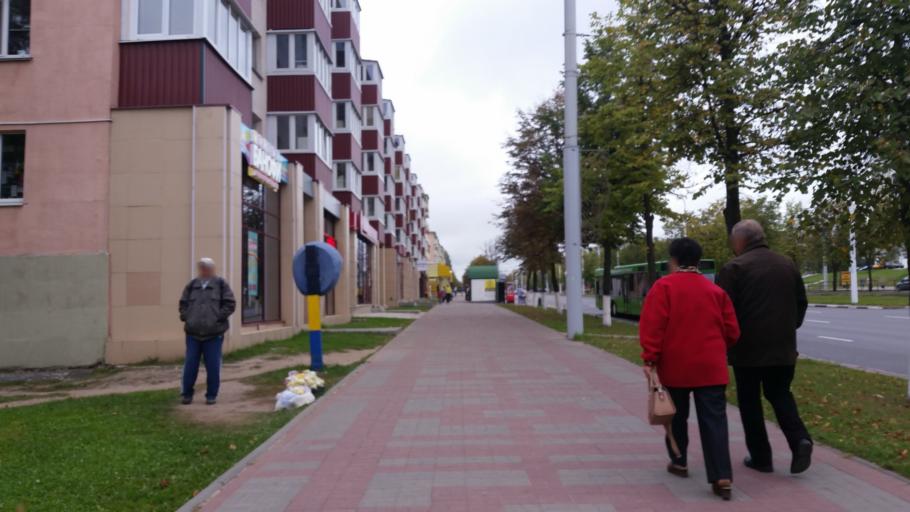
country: BY
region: Vitebsk
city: Vitebsk
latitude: 55.1812
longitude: 30.2133
